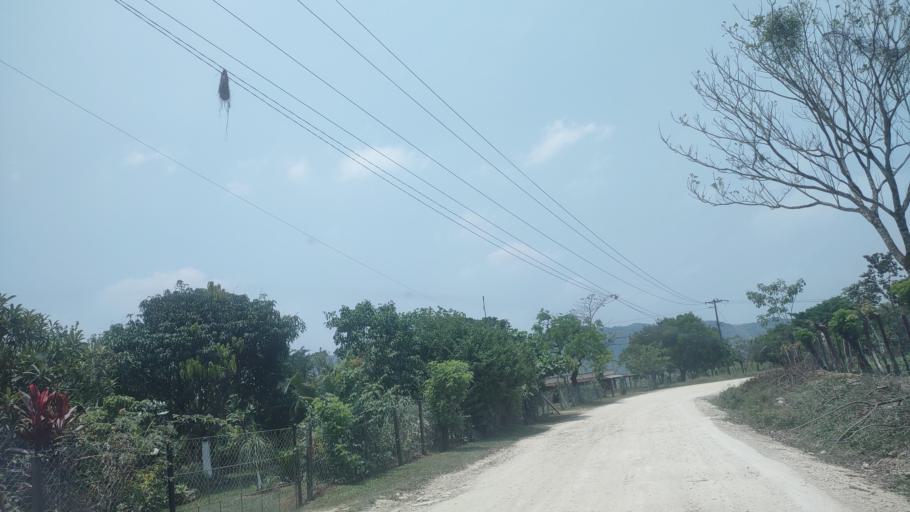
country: MX
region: Chiapas
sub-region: Tecpatan
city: Raudales Malpaso
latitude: 17.4592
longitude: -93.8042
